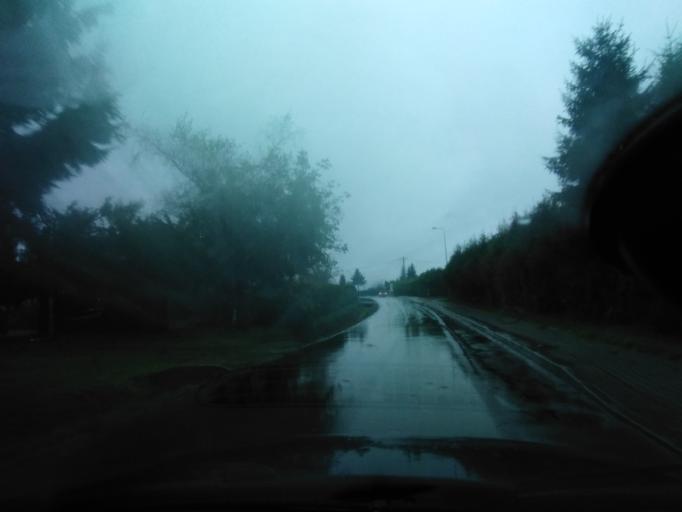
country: PL
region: Subcarpathian Voivodeship
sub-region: Powiat krosnienski
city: Korczyna
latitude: 49.7027
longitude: 21.8125
